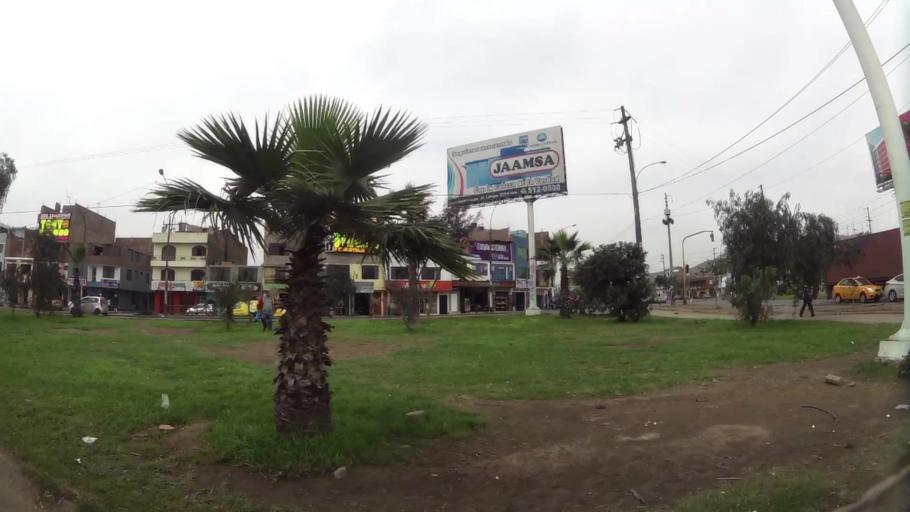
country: PE
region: Lima
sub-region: Lima
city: Independencia
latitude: -12.0123
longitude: -77.0802
